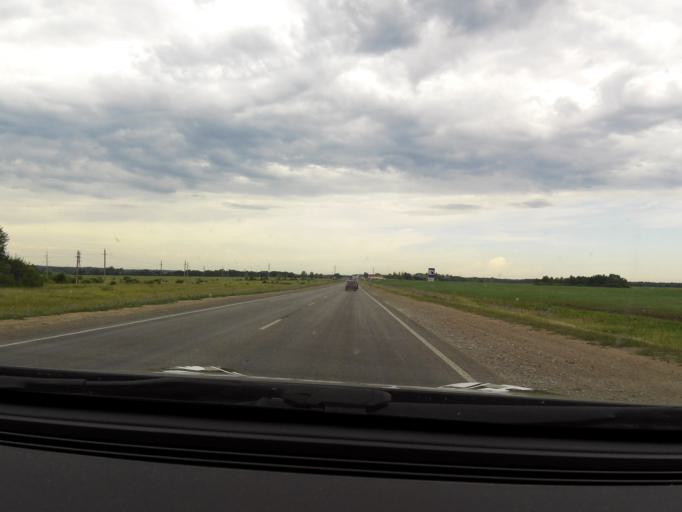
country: RU
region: Bashkortostan
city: Kudeyevskiy
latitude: 54.8169
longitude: 56.7502
